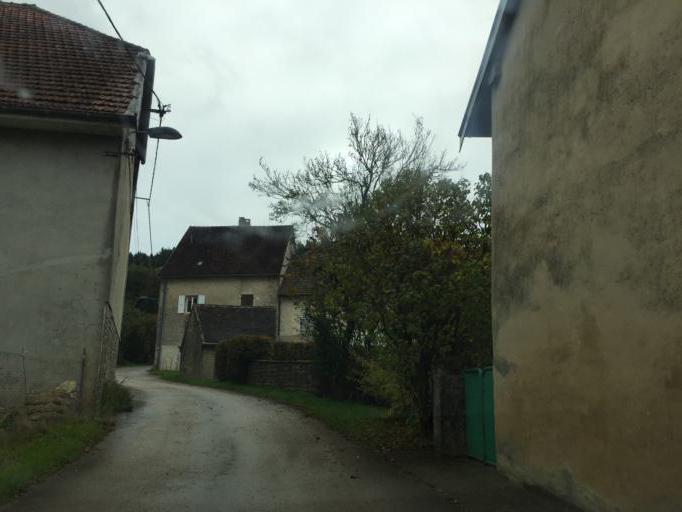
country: FR
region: Franche-Comte
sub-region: Departement du Jura
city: Orgelet
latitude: 46.5165
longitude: 5.5811
